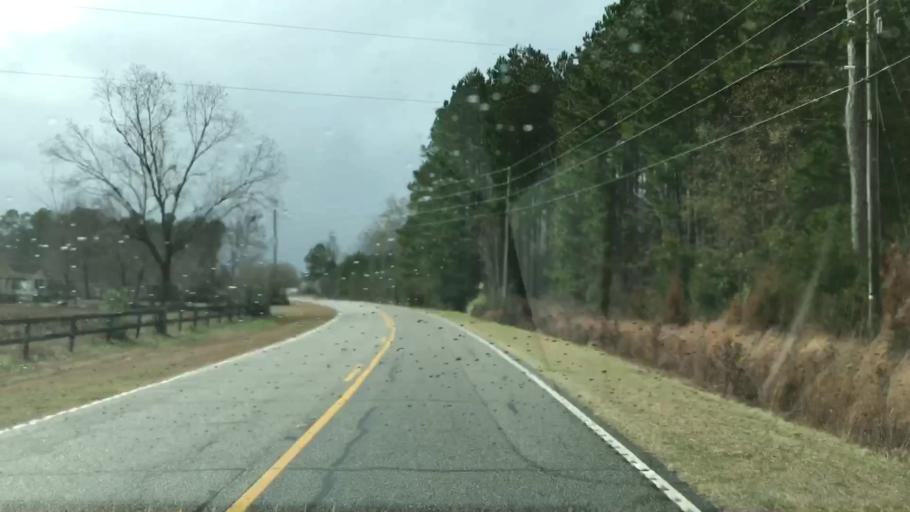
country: US
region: South Carolina
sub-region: Florence County
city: Johnsonville
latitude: 33.6771
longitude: -79.3882
